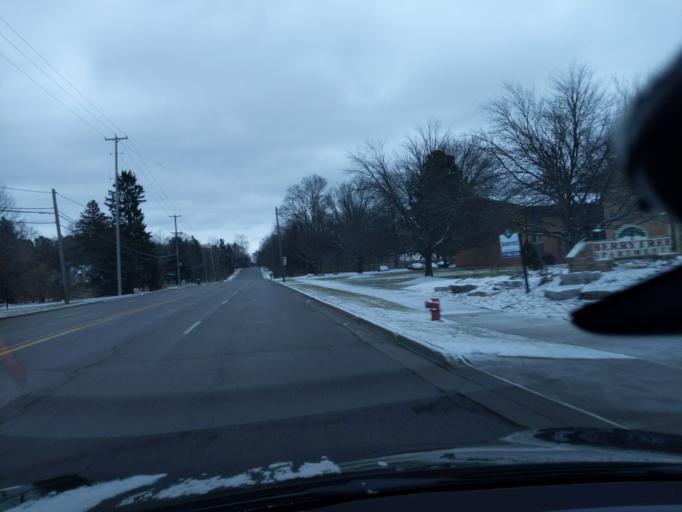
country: US
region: Michigan
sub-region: Ingham County
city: Okemos
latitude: 42.7118
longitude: -84.4592
